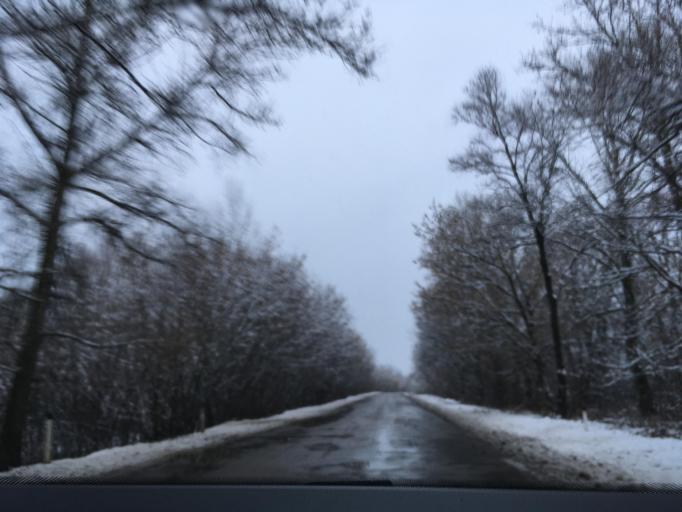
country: RU
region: Voronezj
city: Mitrofanovka
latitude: 50.1336
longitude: 39.9931
